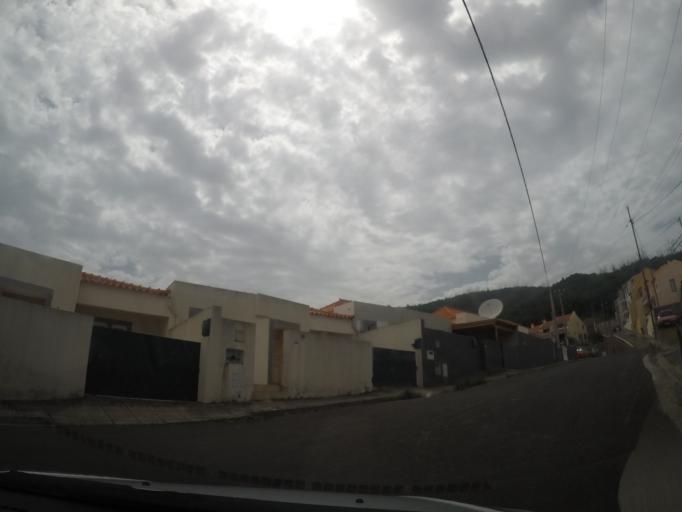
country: PT
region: Madeira
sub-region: Santa Cruz
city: Santa Cruz
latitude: 32.6796
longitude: -16.8087
